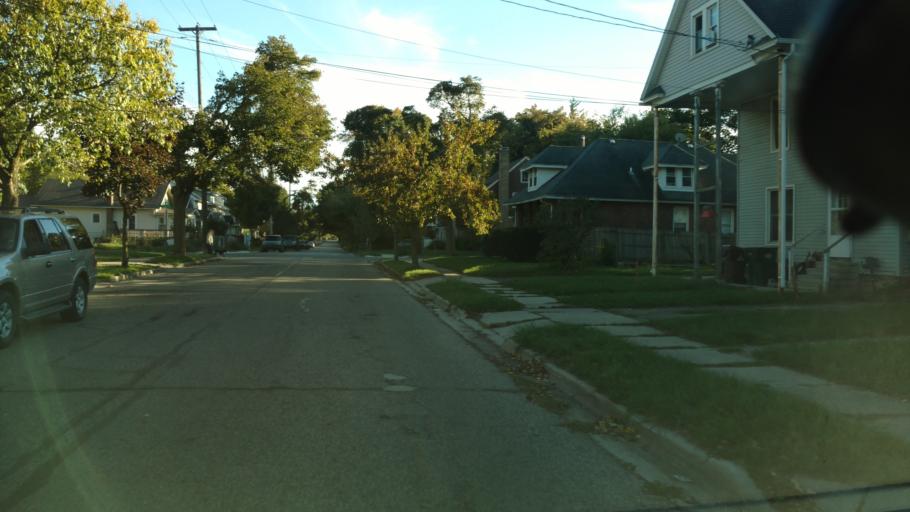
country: US
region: Michigan
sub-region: Ingham County
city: Lansing
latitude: 42.7389
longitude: -84.5212
